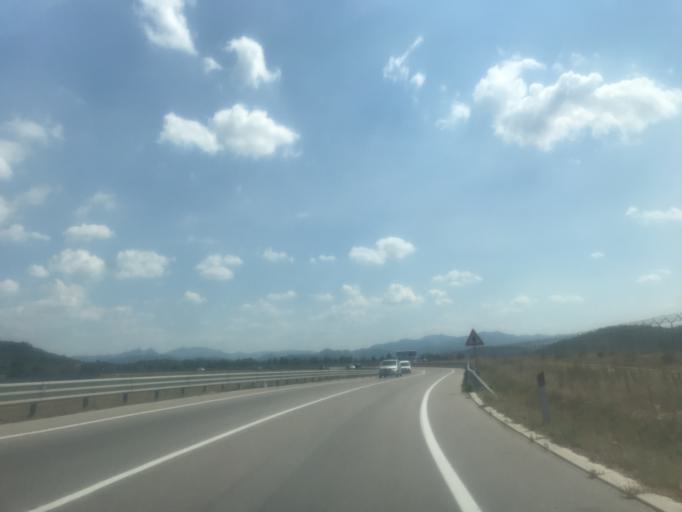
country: IT
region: Sardinia
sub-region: Provincia di Olbia-Tempio
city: Olbia
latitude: 40.9073
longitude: 9.5364
